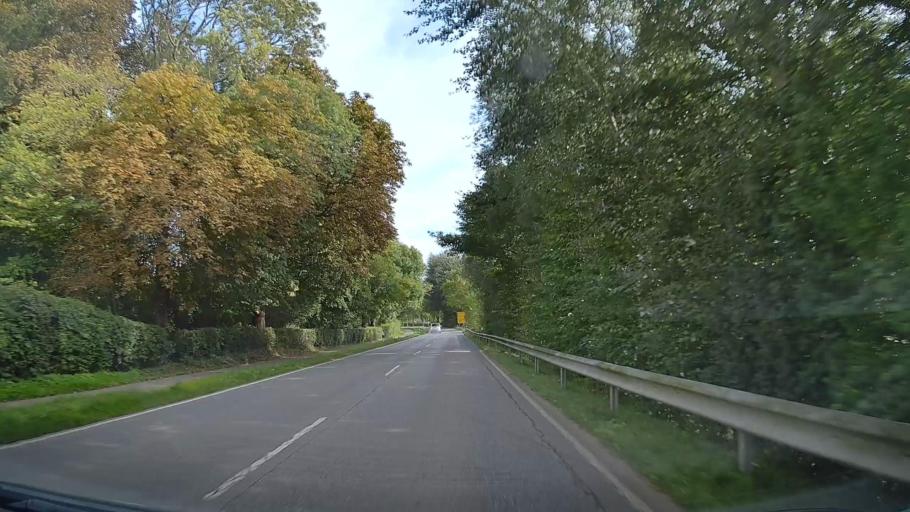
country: DE
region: Schleswig-Holstein
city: Stangheck
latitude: 54.7448
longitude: 9.8701
